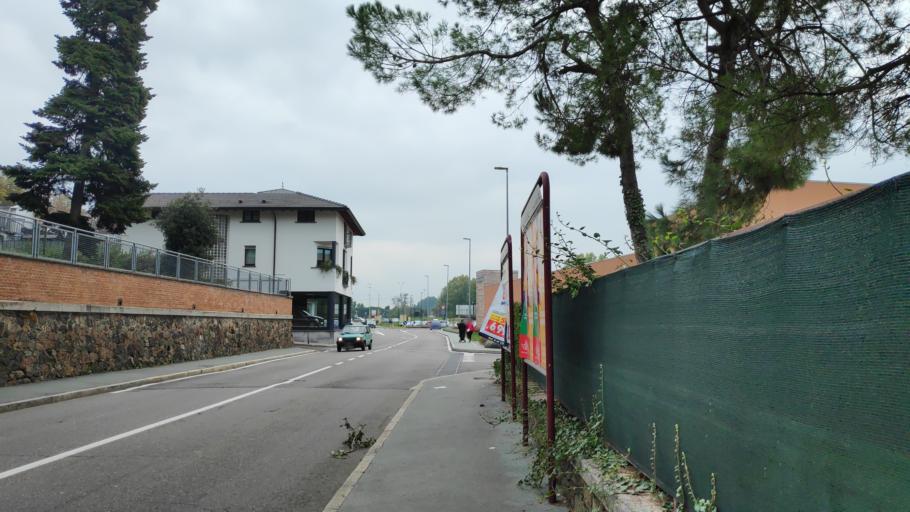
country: IT
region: Lombardy
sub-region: Provincia di Varese
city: Castellanza
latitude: 45.6090
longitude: 8.9068
